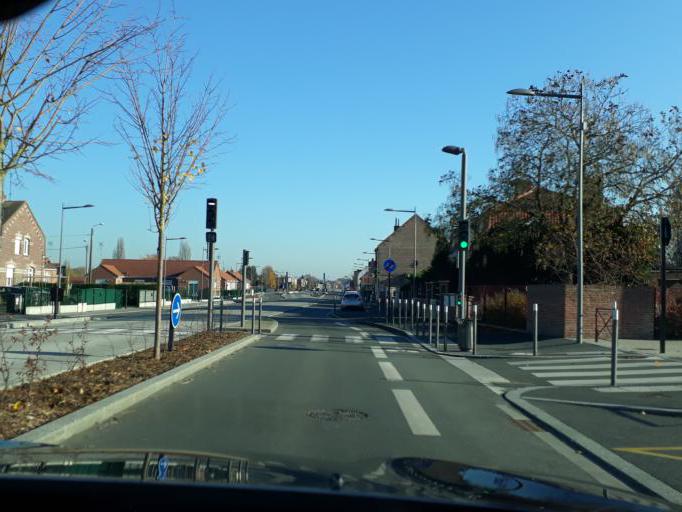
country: FR
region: Nord-Pas-de-Calais
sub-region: Departement du Nord
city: Masny
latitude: 50.3359
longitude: 3.2098
